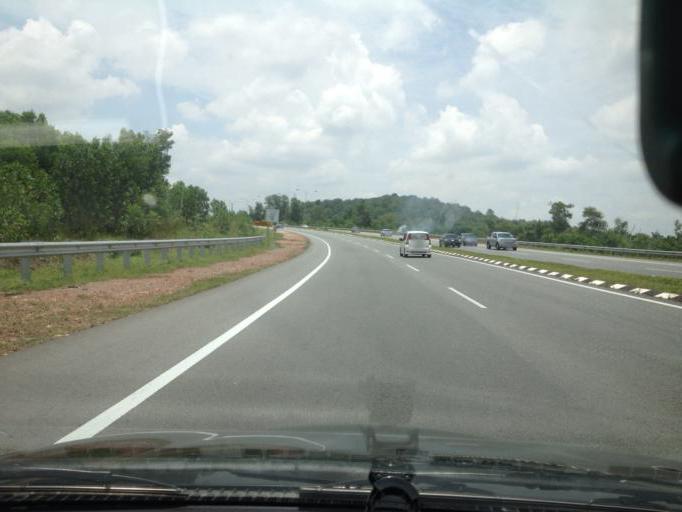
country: MY
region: Kedah
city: Sungai Petani
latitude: 5.6174
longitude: 100.5559
